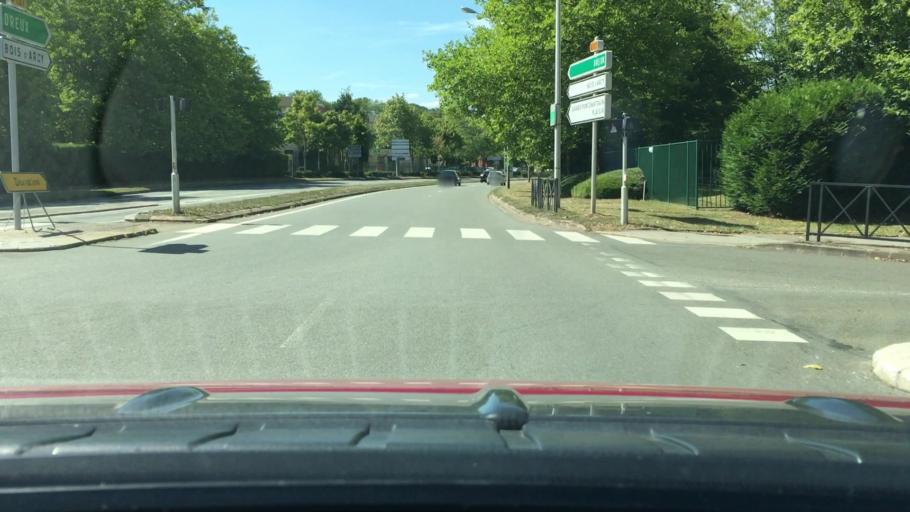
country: FR
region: Ile-de-France
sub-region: Departement des Yvelines
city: Bois-d'Arcy
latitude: 48.7934
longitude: 2.0365
